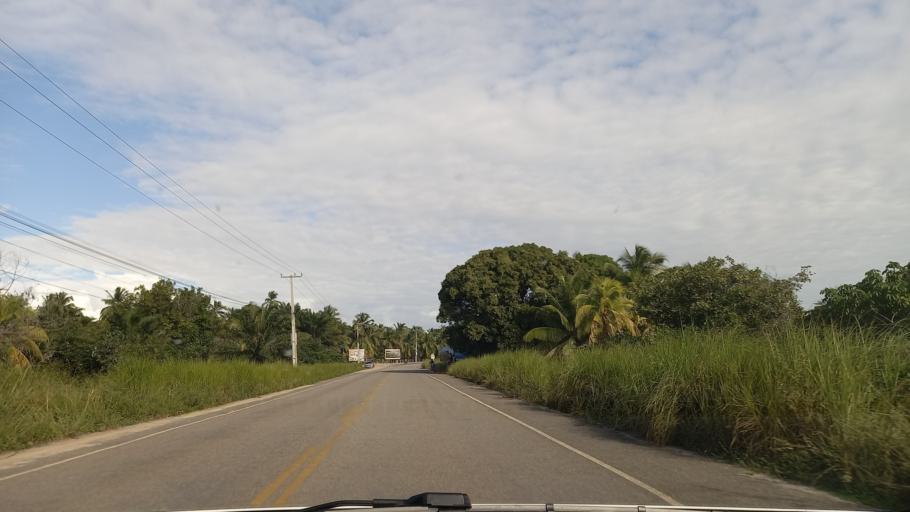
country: BR
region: Pernambuco
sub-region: Tamandare
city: Tamandare
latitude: -8.7042
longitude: -35.0880
